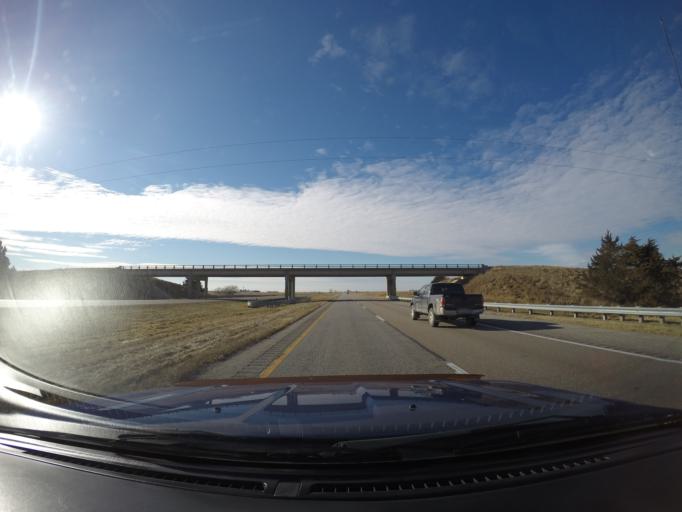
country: US
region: Nebraska
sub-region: Hamilton County
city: Aurora
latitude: 40.8212
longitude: -97.8444
